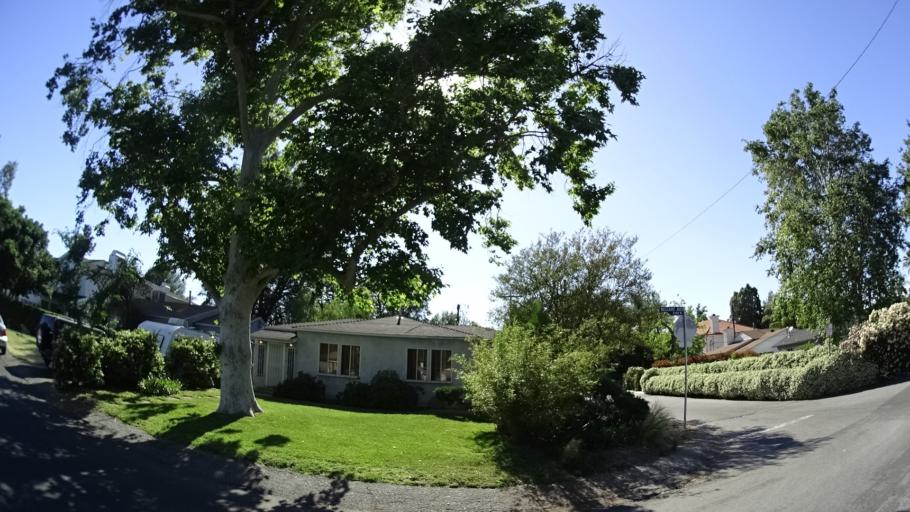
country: US
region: California
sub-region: Los Angeles County
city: North Hollywood
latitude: 34.1665
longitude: -118.4094
